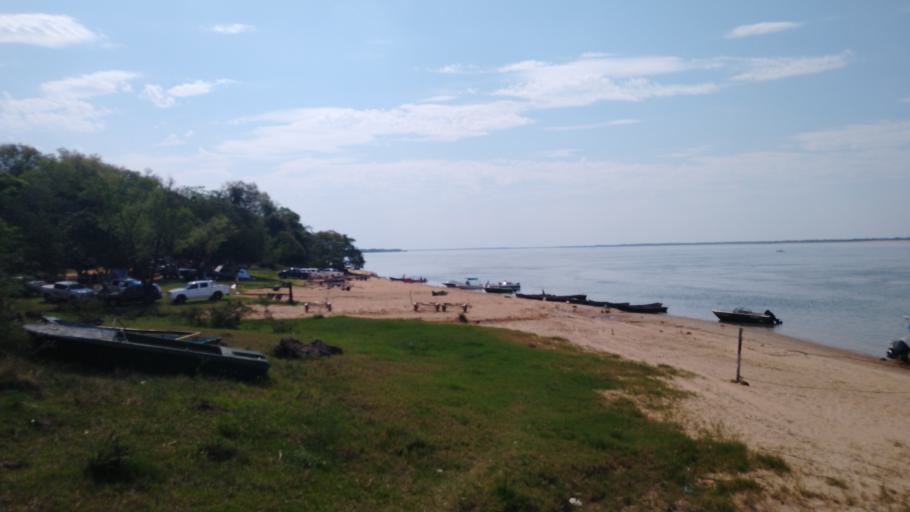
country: PY
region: Neembucu
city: Cerrito
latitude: -27.3694
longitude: -57.6554
